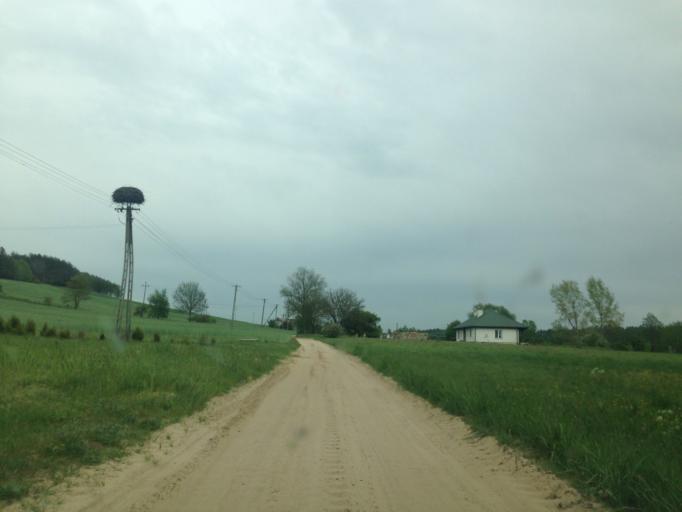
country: PL
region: Kujawsko-Pomorskie
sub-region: Powiat brodnicki
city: Bartniczka
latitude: 53.2802
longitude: 19.5951
